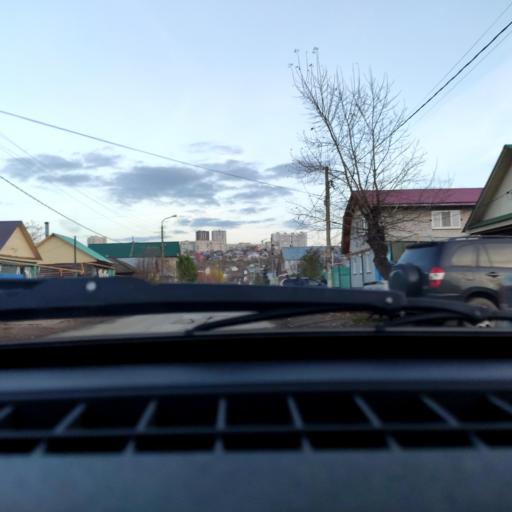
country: RU
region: Bashkortostan
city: Ufa
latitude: 54.7407
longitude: 55.9172
